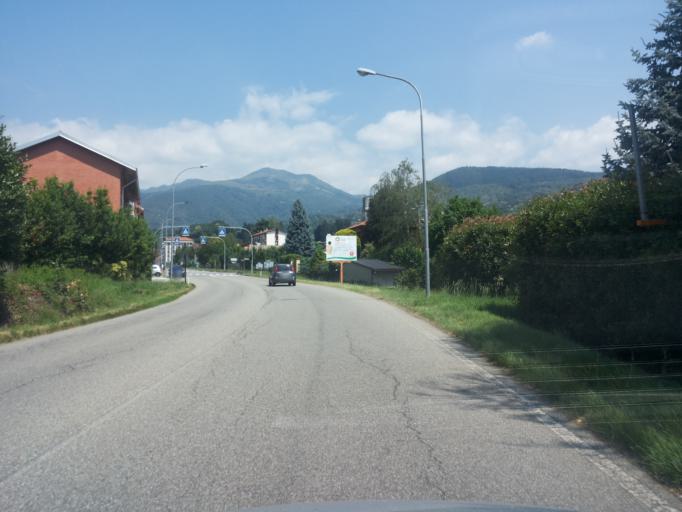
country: IT
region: Piedmont
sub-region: Provincia di Biella
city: Andorno Cacciorna
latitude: 45.6085
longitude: 8.0534
